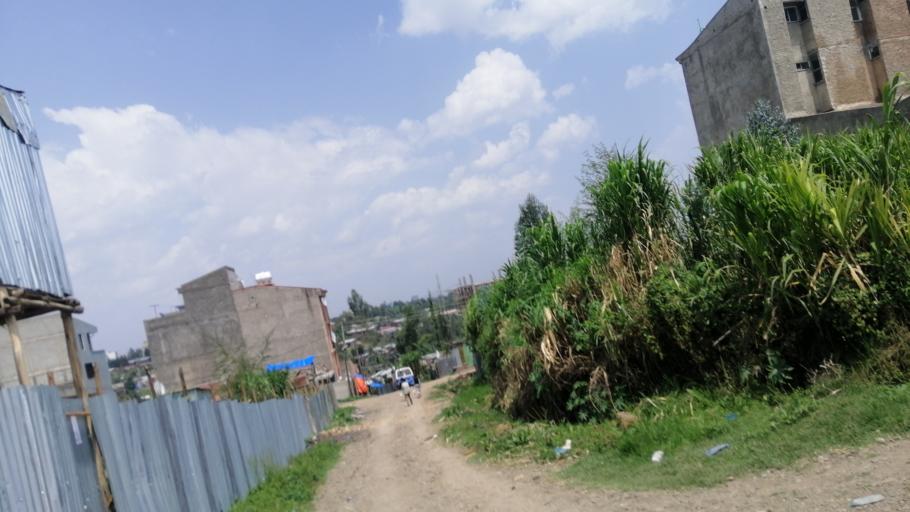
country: ET
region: Adis Abeba
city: Addis Ababa
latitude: 8.9426
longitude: 38.7568
